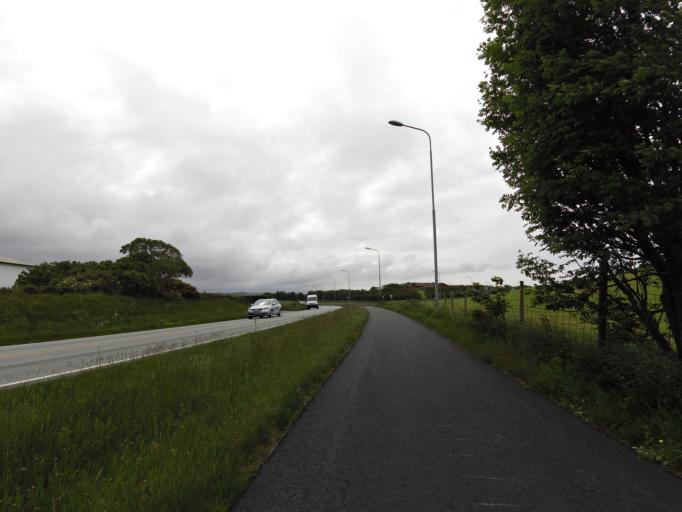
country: NO
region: Rogaland
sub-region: Klepp
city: Kleppe
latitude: 58.8222
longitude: 5.5884
